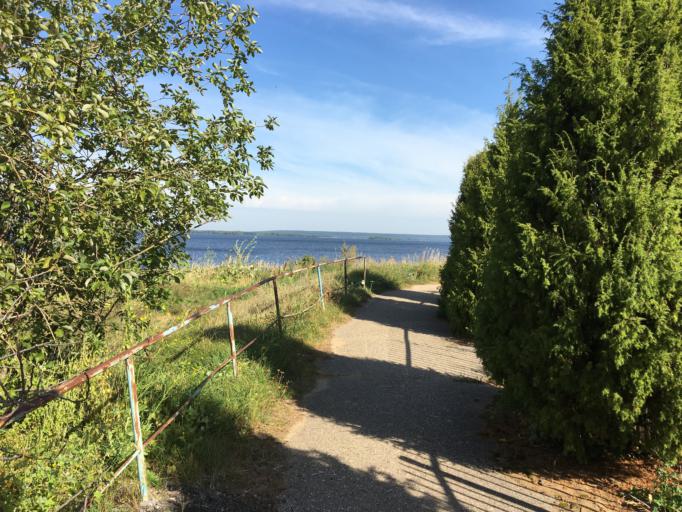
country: RU
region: Chuvashia
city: Ishley
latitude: 56.1312
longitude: 47.0439
